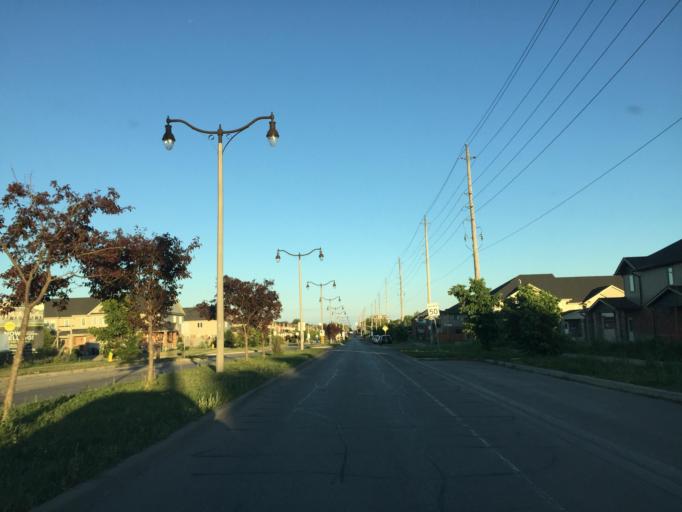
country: CA
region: Ontario
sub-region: Wellington County
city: Guelph
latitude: 43.5823
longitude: -80.2663
